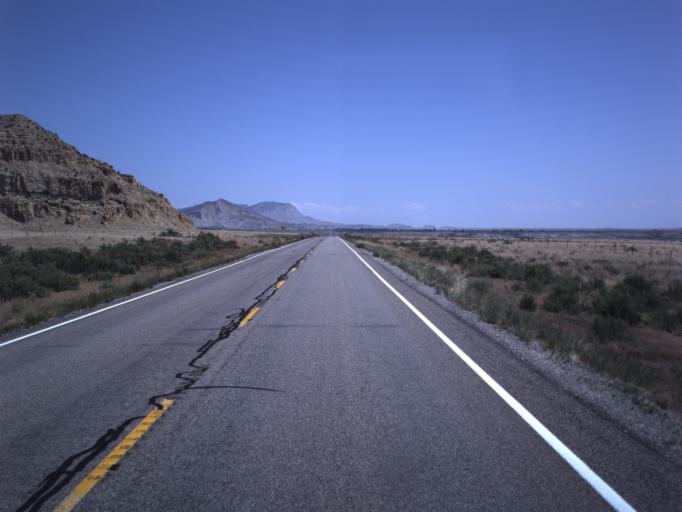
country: US
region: Utah
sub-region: Emery County
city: Ferron
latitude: 38.8315
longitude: -111.3209
